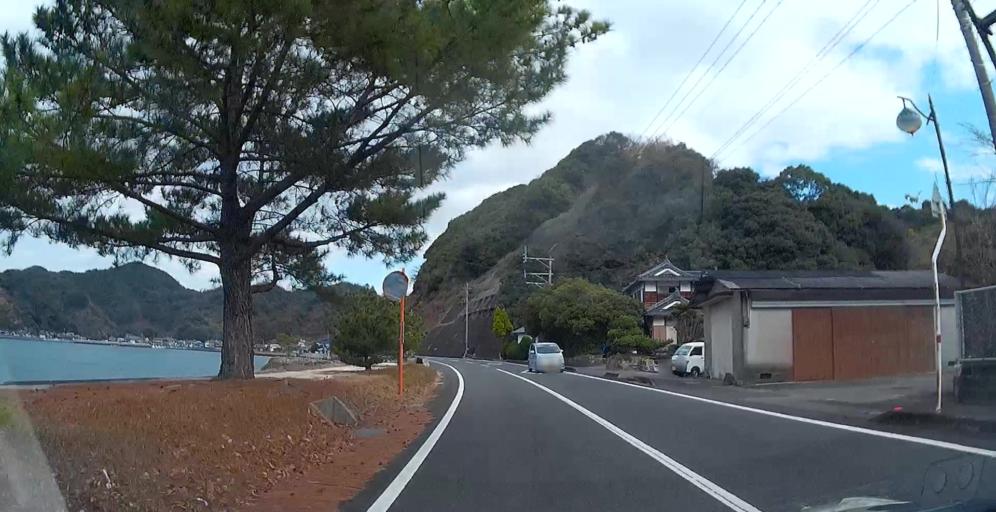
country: JP
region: Kumamoto
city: Minamata
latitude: 32.3277
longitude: 130.4825
